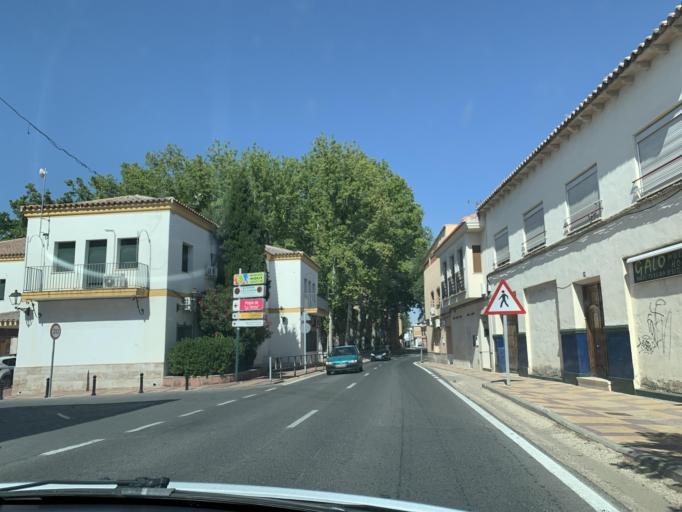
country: ES
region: Castille-La Mancha
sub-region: Provincia de Ciudad Real
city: Argamasilla de Alba
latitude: 39.1283
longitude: -3.0904
